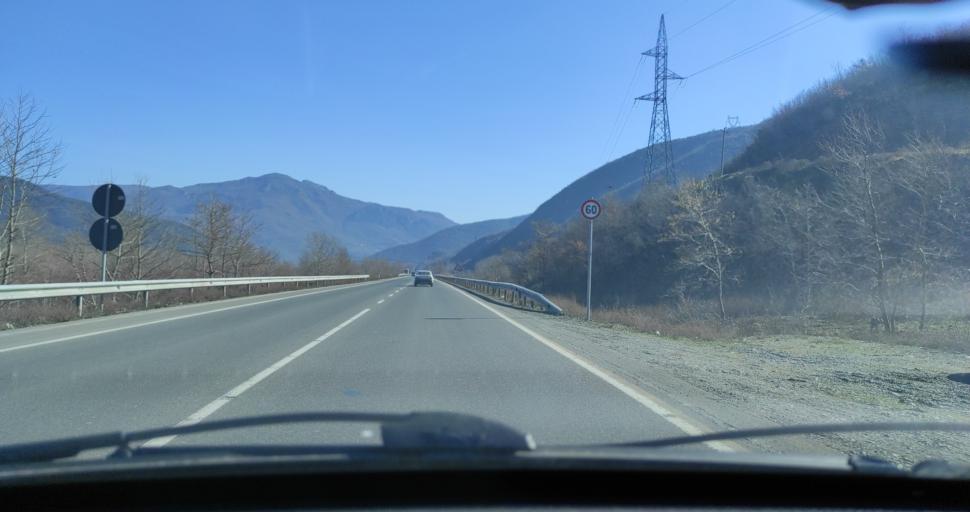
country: AL
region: Lezhe
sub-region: Rrethi i Kurbinit
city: Milot
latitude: 41.6982
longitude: 19.7402
